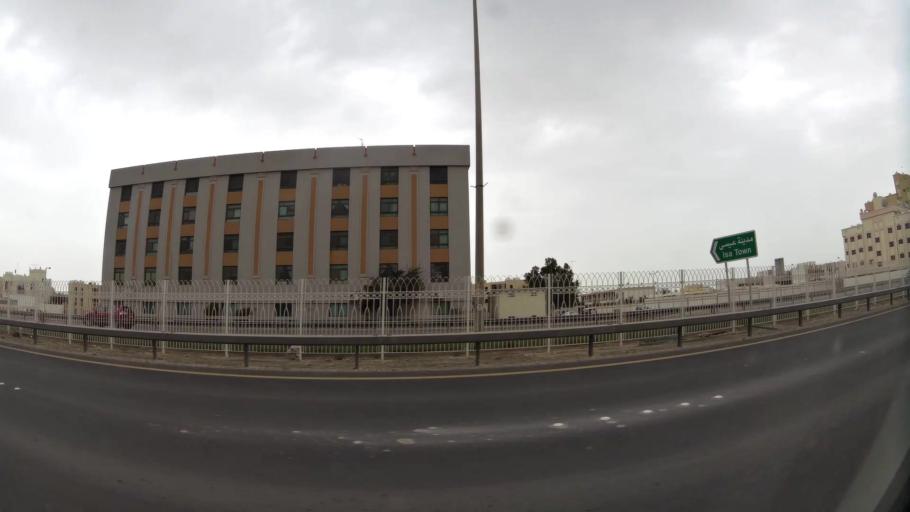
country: BH
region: Northern
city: Madinat `Isa
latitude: 26.1632
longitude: 50.5592
